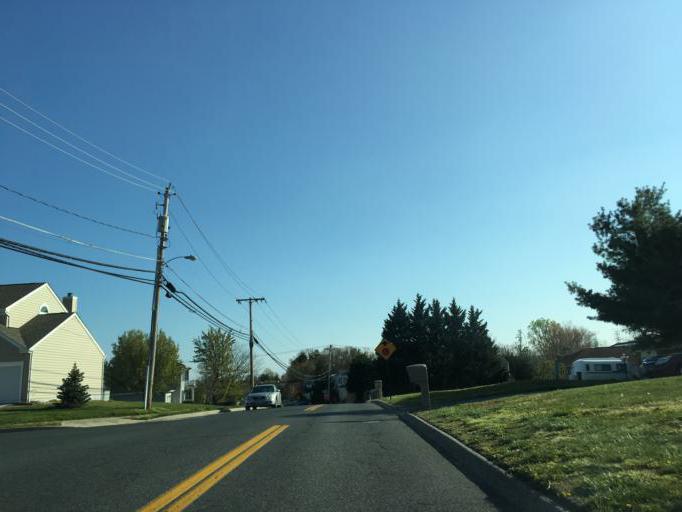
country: US
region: Maryland
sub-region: Baltimore County
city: Carney
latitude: 39.4043
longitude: -76.4965
